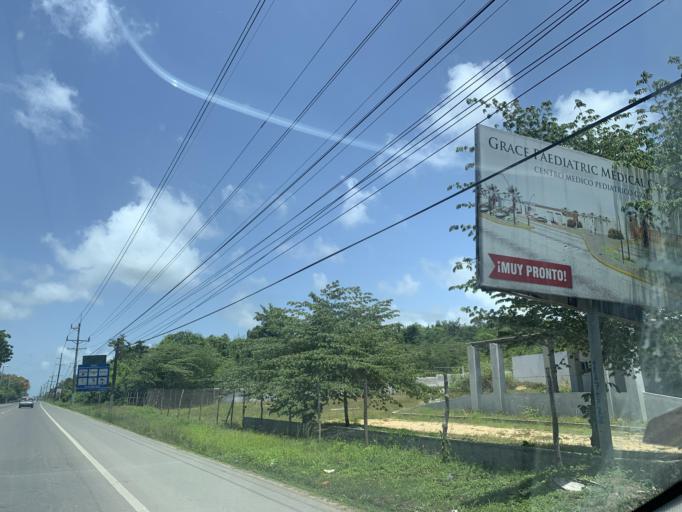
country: DO
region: Puerto Plata
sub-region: Puerto Plata
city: Puerto Plata
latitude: 19.7502
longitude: -70.5707
